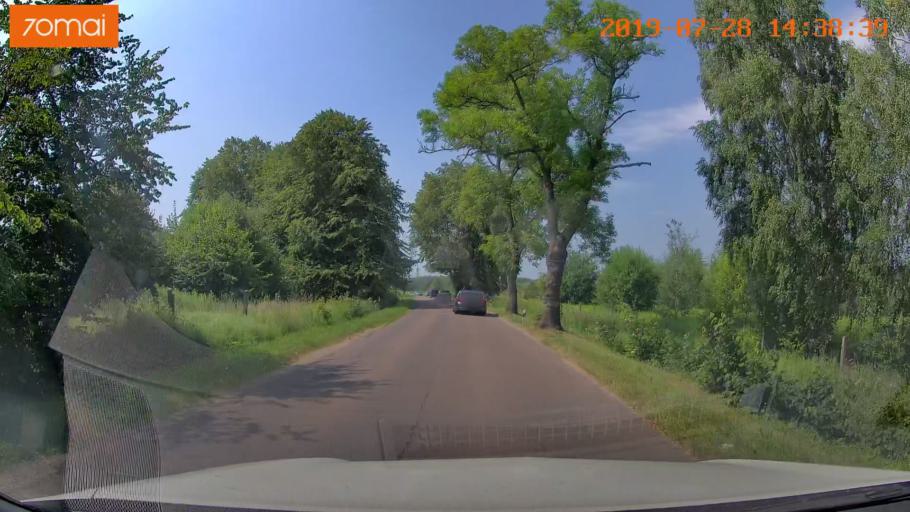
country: RU
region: Kaliningrad
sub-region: Gorod Kaliningrad
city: Yantarnyy
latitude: 54.8455
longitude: 19.9811
